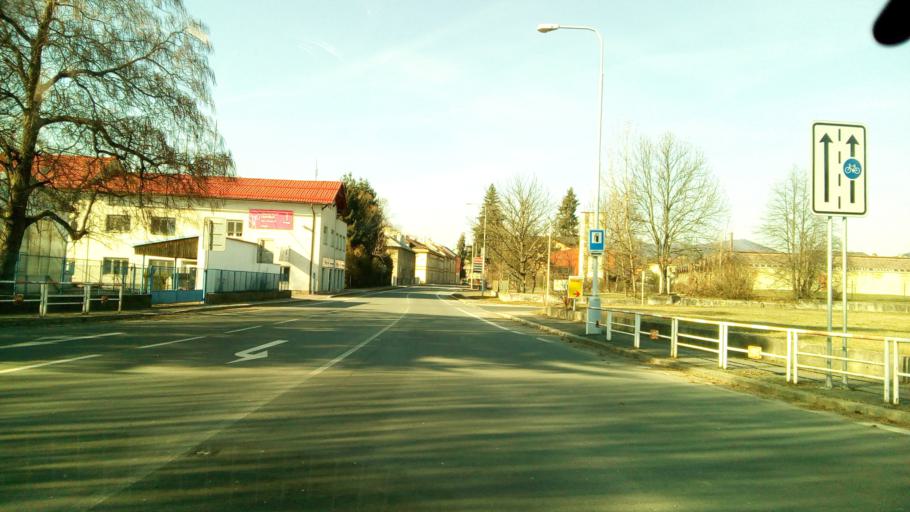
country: CZ
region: Olomoucky
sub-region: Okres Sumperk
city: Sumperk
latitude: 49.9595
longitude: 16.9750
